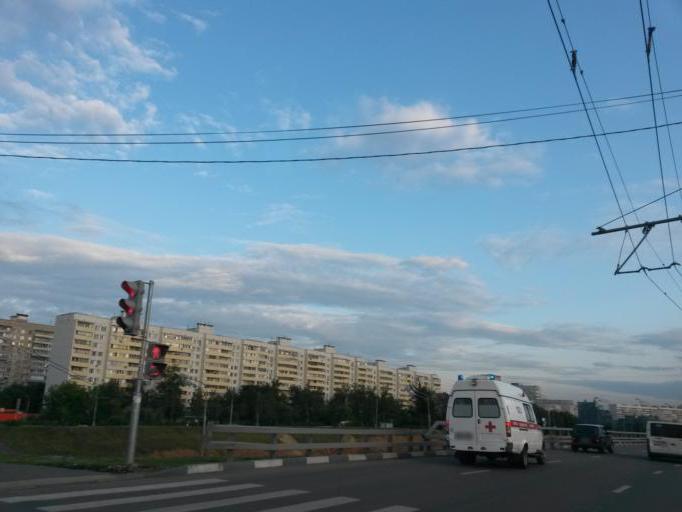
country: RU
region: Moscow
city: Chertanovo Yuzhnoye
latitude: 55.6101
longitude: 37.6082
